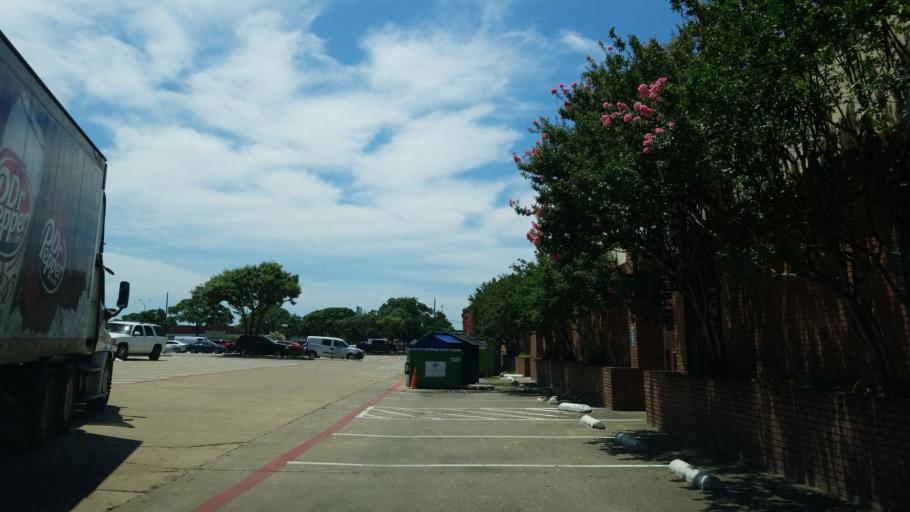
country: US
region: Texas
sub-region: Dallas County
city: Farmers Branch
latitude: 32.9109
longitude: -96.8536
